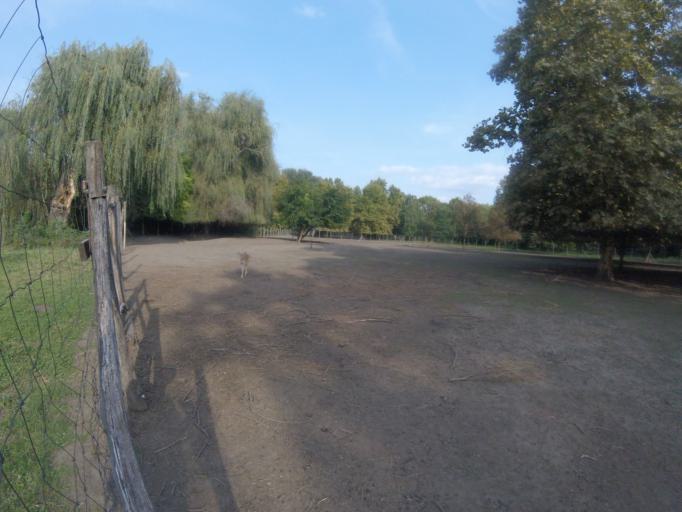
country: HU
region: Komarom-Esztergom
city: Babolna
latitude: 47.6423
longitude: 17.9869
